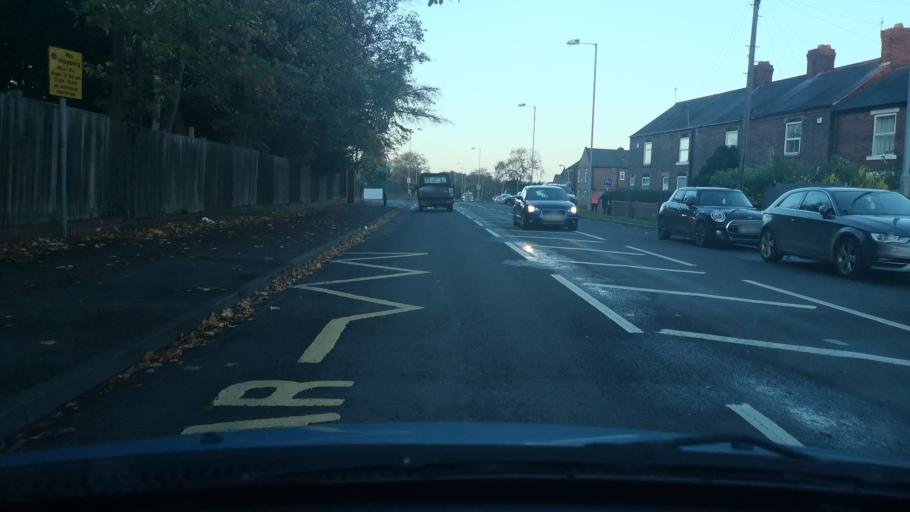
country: GB
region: England
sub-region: City and Borough of Wakefield
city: Horbury
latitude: 53.6595
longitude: -1.5461
